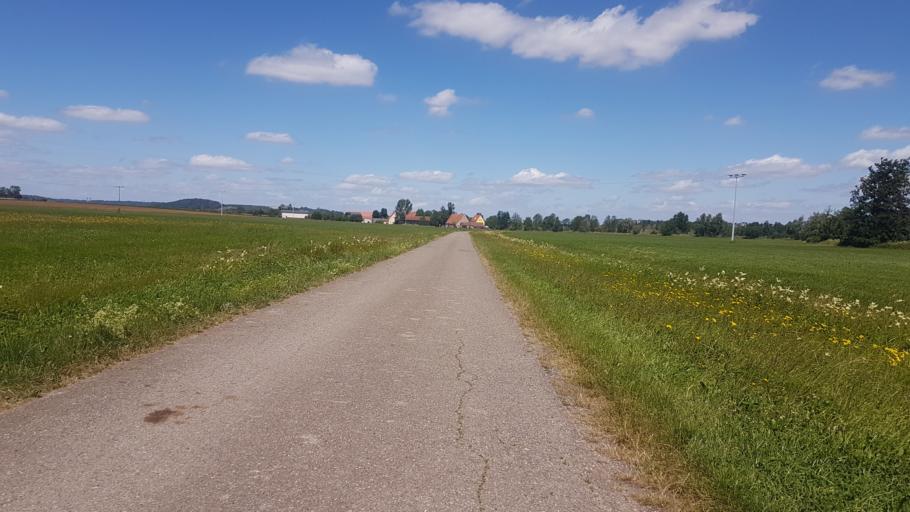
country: DE
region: Bavaria
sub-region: Regierungsbezirk Mittelfranken
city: Leutershausen
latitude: 49.2763
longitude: 10.4288
